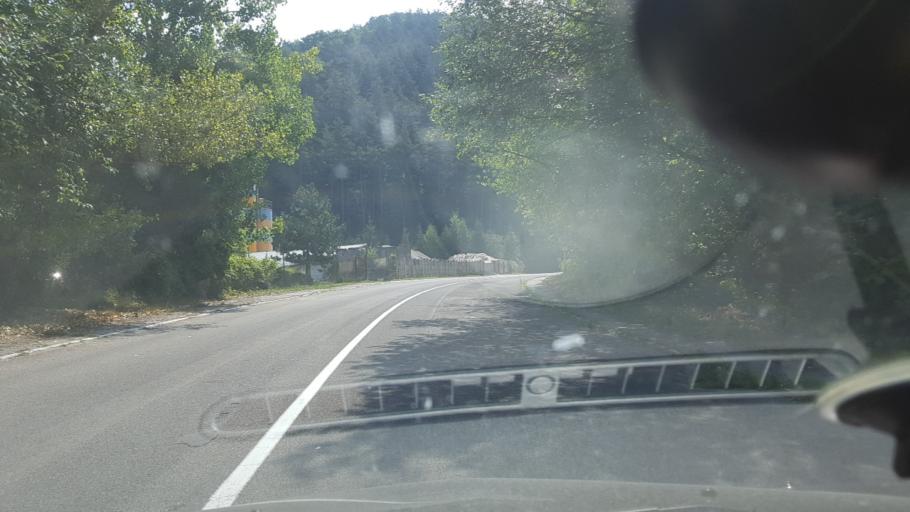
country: SK
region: Banskobystricky
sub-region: Okres Banska Bystrica
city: Banska Bystrica
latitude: 48.7281
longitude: 19.1642
